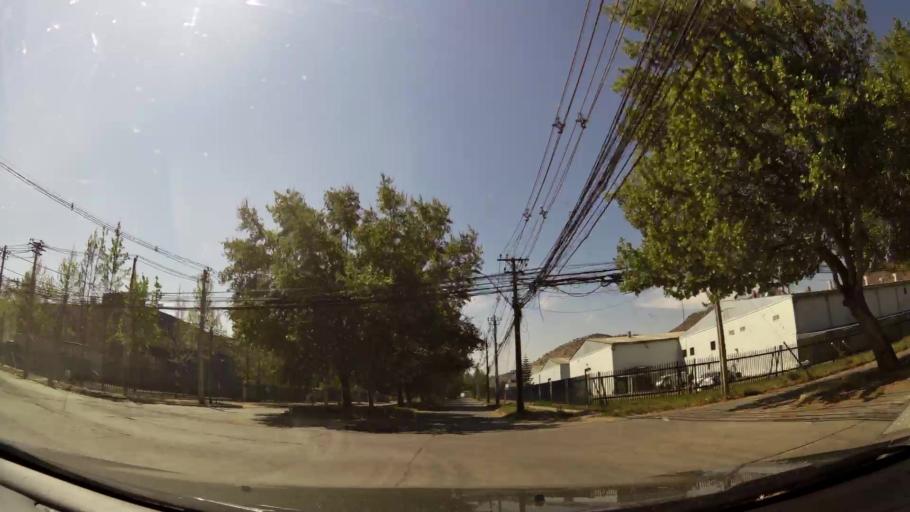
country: CL
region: Santiago Metropolitan
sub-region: Provincia de Santiago
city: Lo Prado
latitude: -33.3827
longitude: -70.7465
